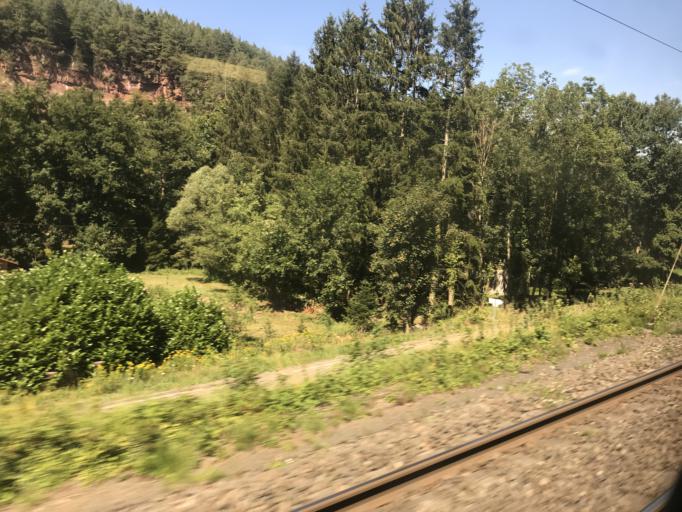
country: FR
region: Alsace
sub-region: Departement du Bas-Rhin
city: Saverne
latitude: 48.7208
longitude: 7.3179
